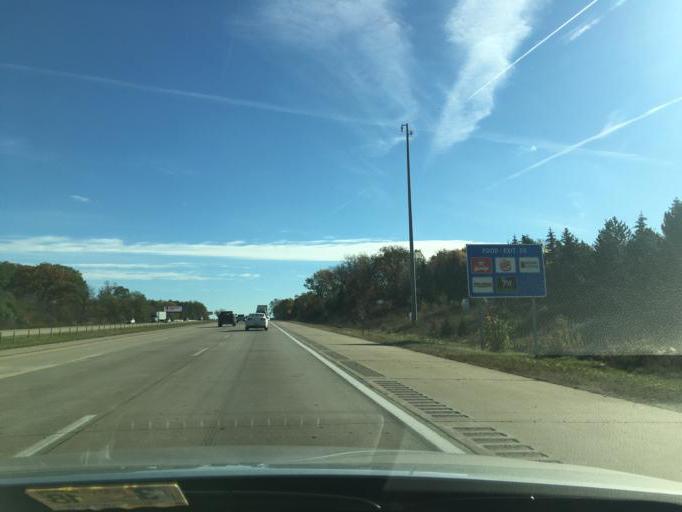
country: US
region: Michigan
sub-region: Wayne County
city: Plymouth
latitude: 42.3827
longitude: -83.4933
